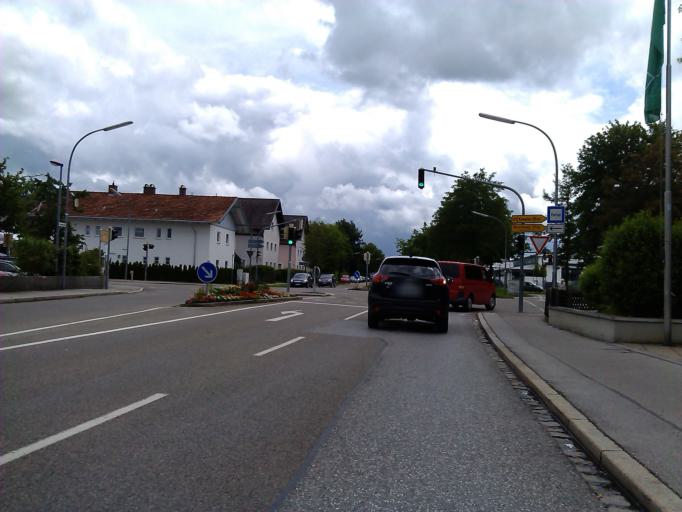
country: DE
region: Bavaria
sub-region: Swabia
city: Marktoberdorf
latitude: 47.7747
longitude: 10.6144
